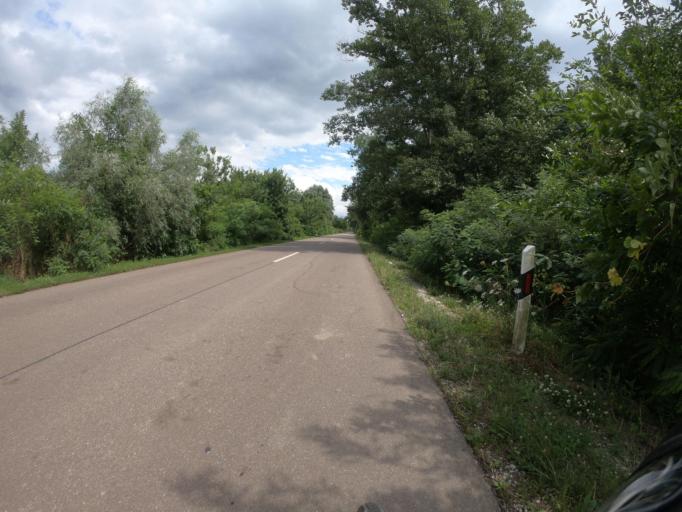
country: HU
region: Jasz-Nagykun-Szolnok
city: Tiszafured
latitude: 47.6907
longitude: 20.7716
